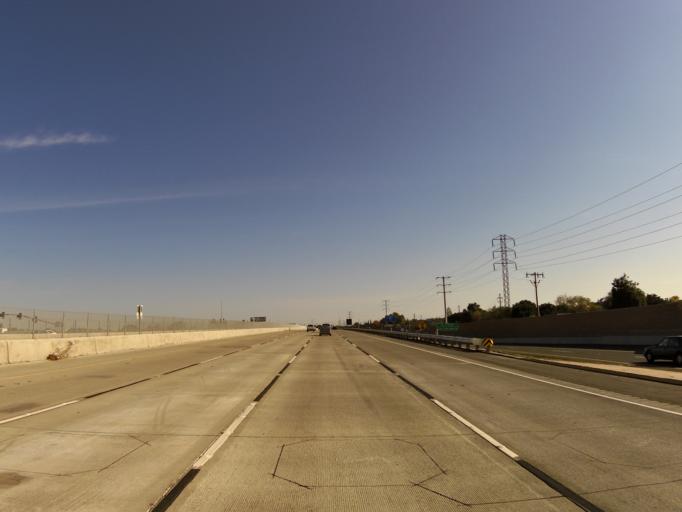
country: US
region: California
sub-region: Contra Costa County
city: Antioch
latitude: 37.9982
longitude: -121.8092
